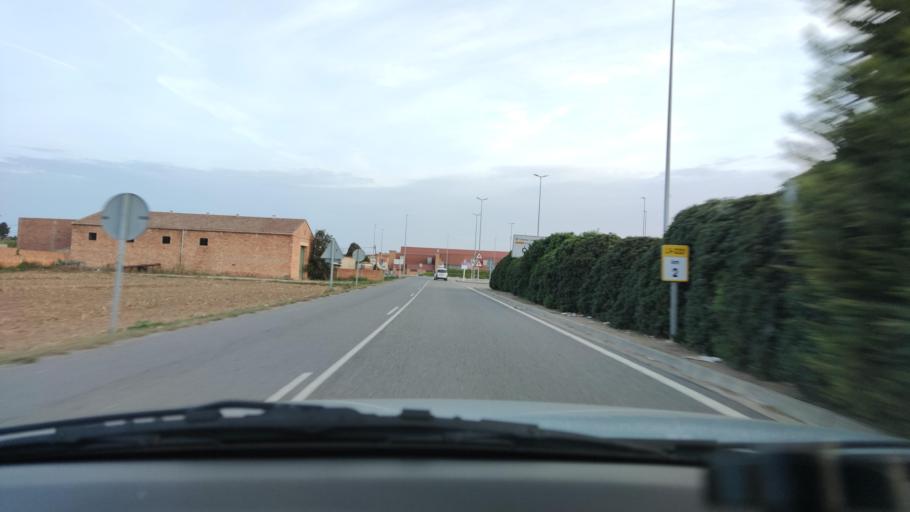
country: ES
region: Catalonia
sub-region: Provincia de Lleida
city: Mollerussa
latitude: 41.6463
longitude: 0.8770
